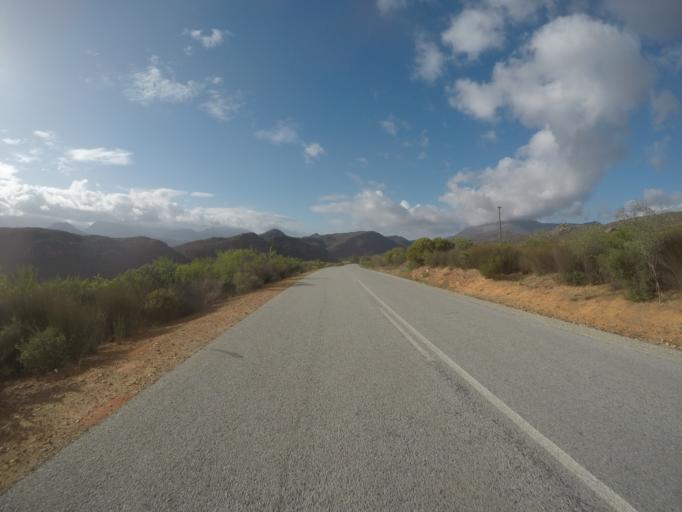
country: ZA
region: Western Cape
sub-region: West Coast District Municipality
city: Clanwilliam
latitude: -32.4272
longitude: 18.9369
